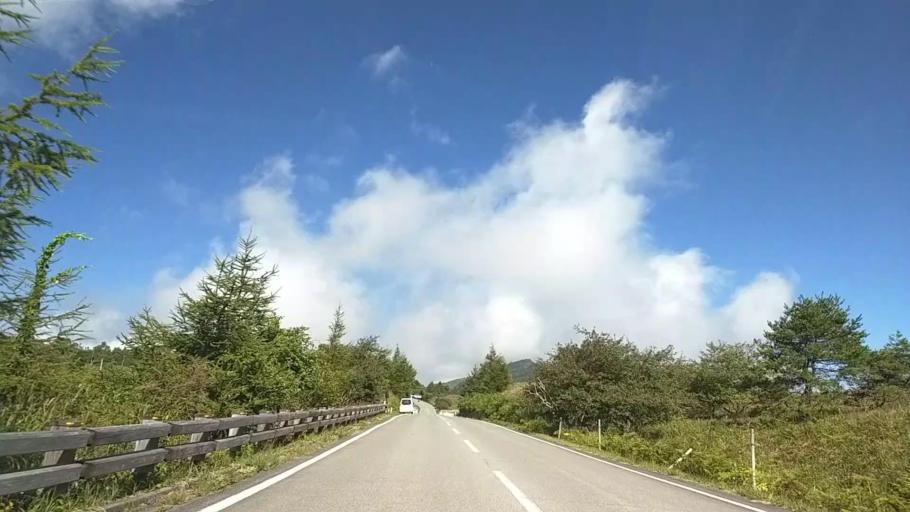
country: JP
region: Nagano
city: Suwa
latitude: 36.1128
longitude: 138.1655
